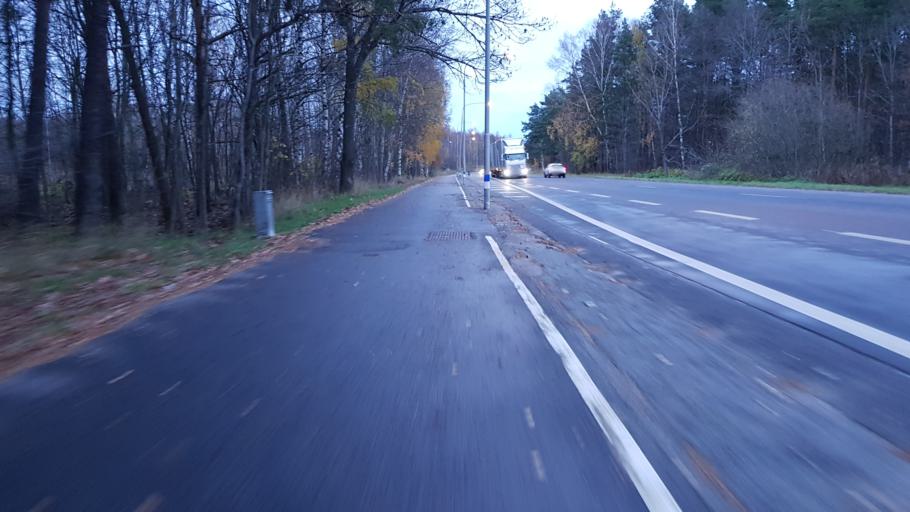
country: SE
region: OEstergoetland
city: Lindo
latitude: 58.5956
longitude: 16.2325
